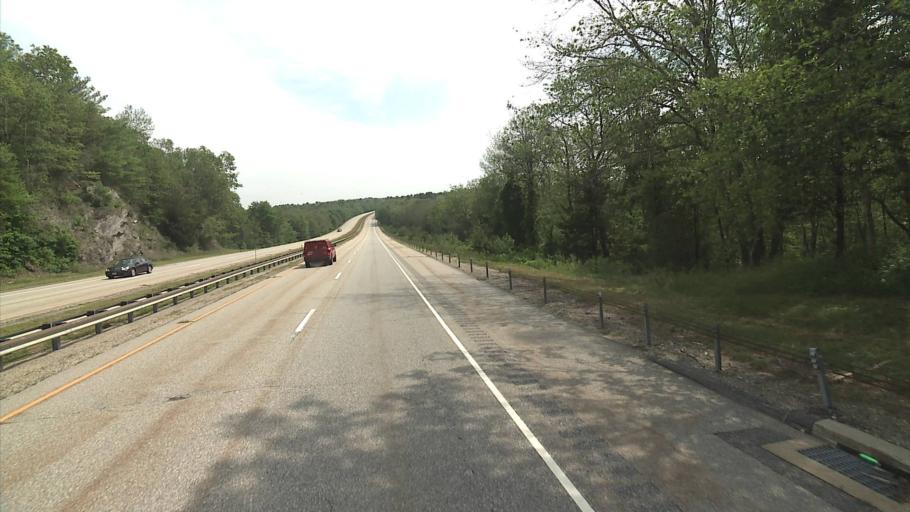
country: US
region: Connecticut
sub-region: Windham County
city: Danielson
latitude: 41.7746
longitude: -71.8505
